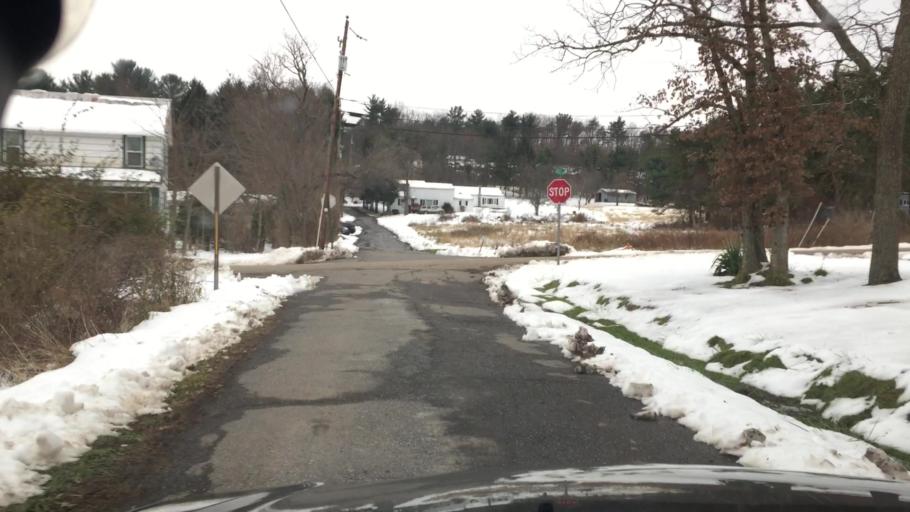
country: US
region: Pennsylvania
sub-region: Luzerne County
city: Nescopeck
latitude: 41.0022
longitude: -76.1492
